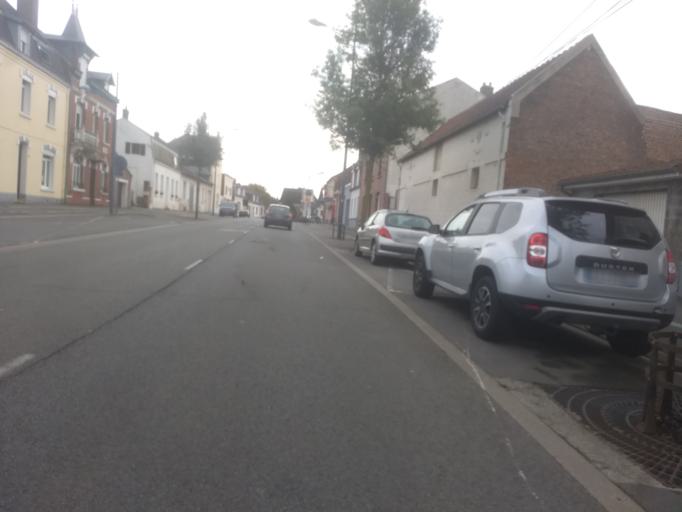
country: FR
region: Nord-Pas-de-Calais
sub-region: Departement du Pas-de-Calais
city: Beaurains
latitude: 50.2675
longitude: 2.7848
